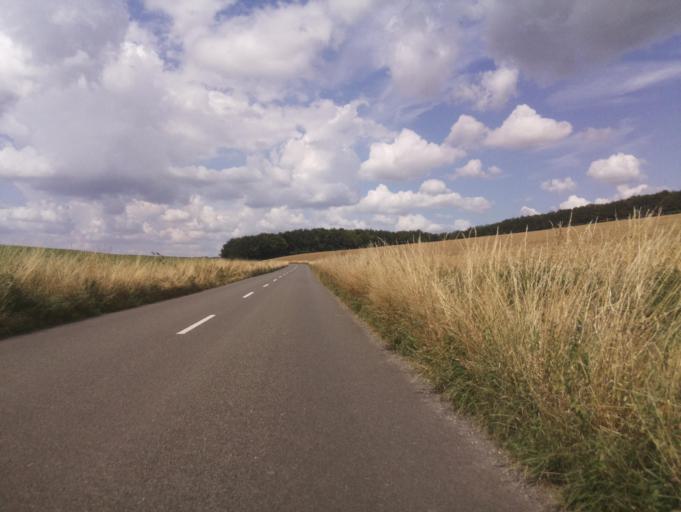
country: GB
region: England
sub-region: Borough of Swindon
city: Bishopstone
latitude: 51.5480
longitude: -1.5953
